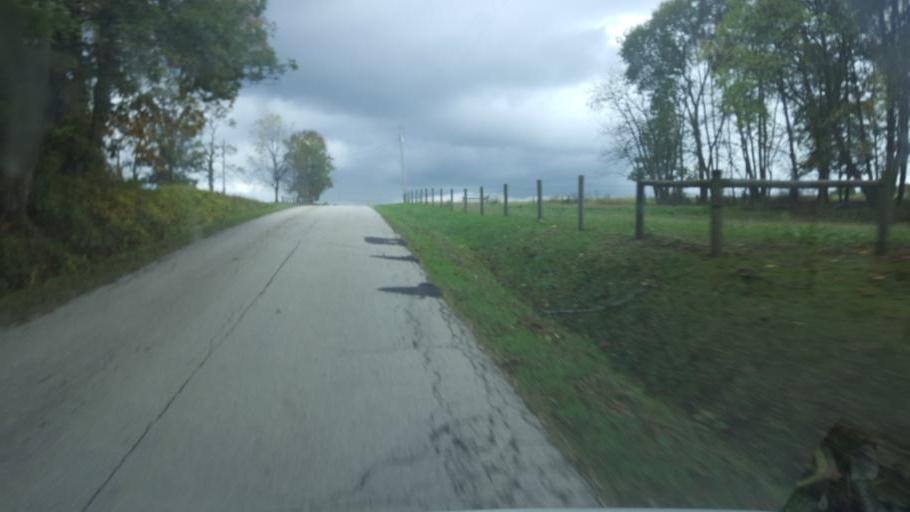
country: US
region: Ohio
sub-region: Ashland County
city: Loudonville
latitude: 40.5618
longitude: -82.1622
